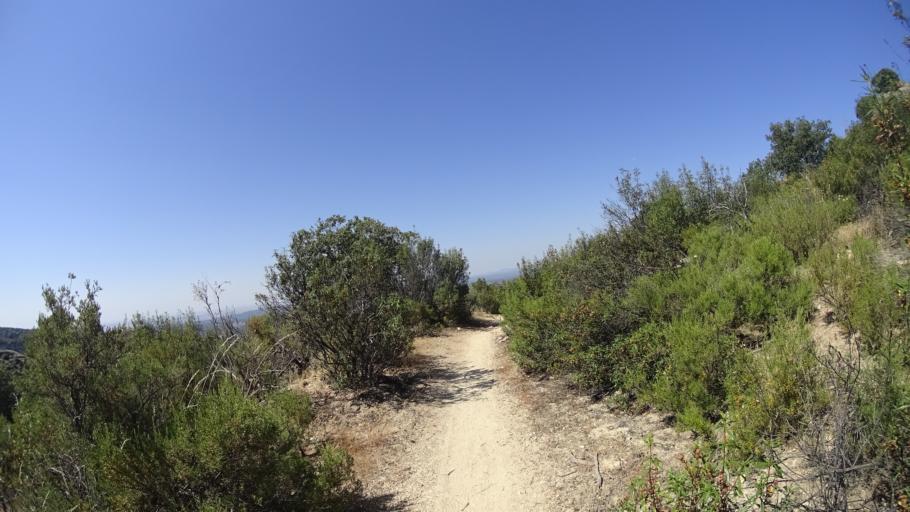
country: ES
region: Madrid
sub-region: Provincia de Madrid
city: Hoyo de Manzanares
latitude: 40.6426
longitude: -3.9378
